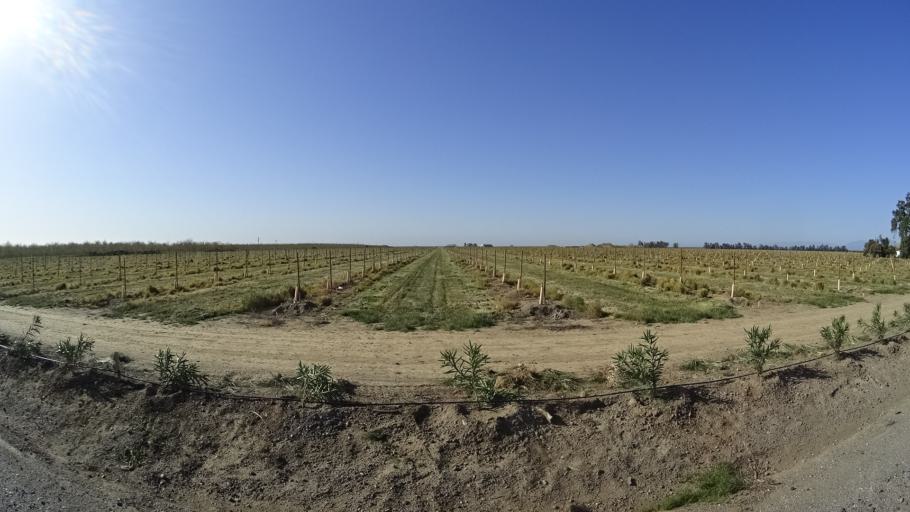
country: US
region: California
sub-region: Glenn County
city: Hamilton City
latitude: 39.6959
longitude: -122.0857
